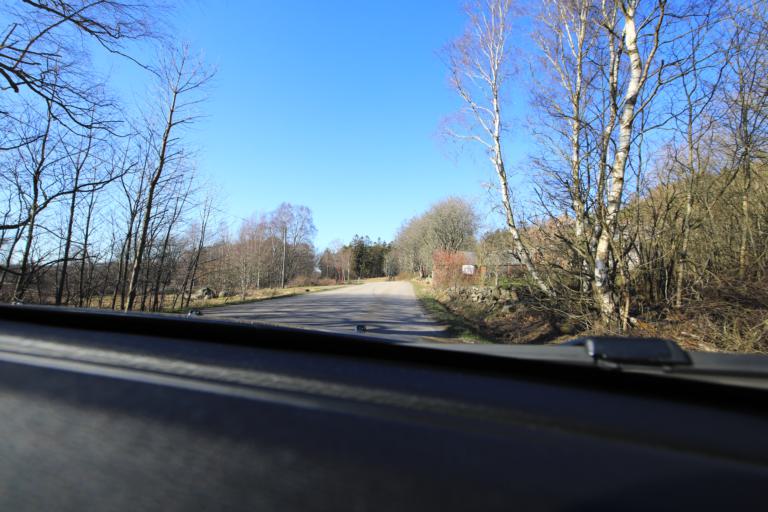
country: SE
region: Halland
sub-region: Varbergs Kommun
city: Tvaaker
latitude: 57.0622
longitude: 12.4248
